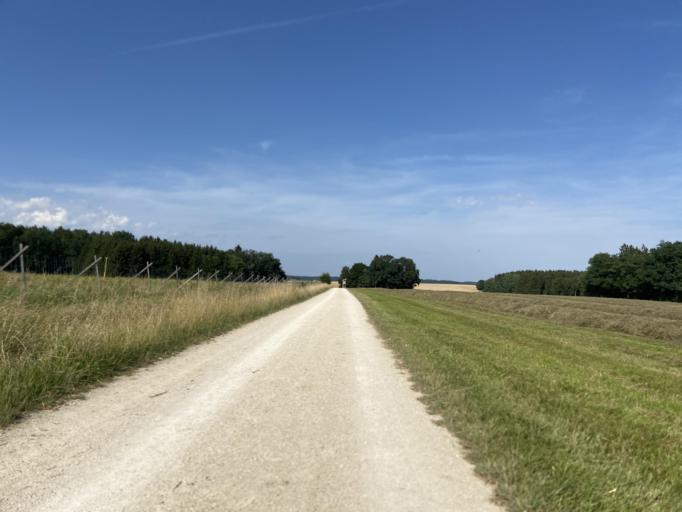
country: DE
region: Baden-Wuerttemberg
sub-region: Tuebingen Region
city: Bingen
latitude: 48.0938
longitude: 9.2602
